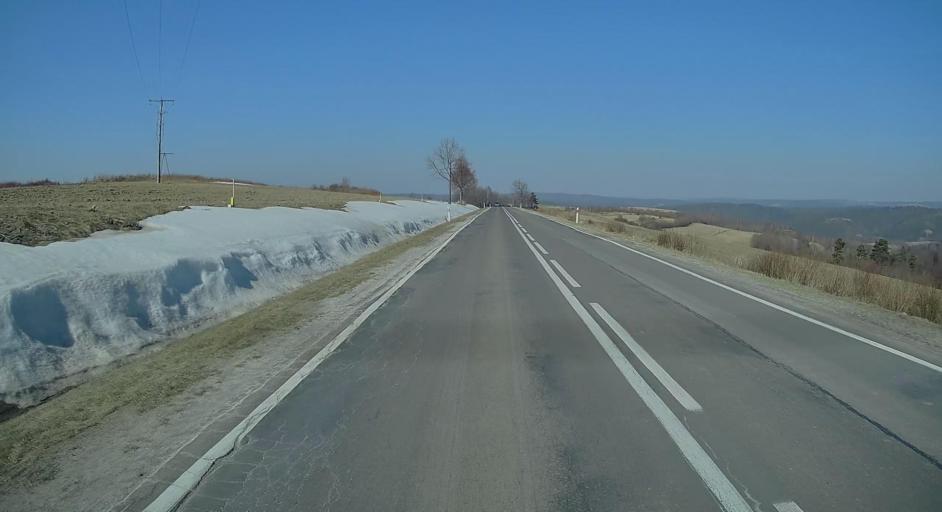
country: PL
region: Subcarpathian Voivodeship
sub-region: Powiat przemyski
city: Bircza
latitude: 49.6373
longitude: 22.4232
